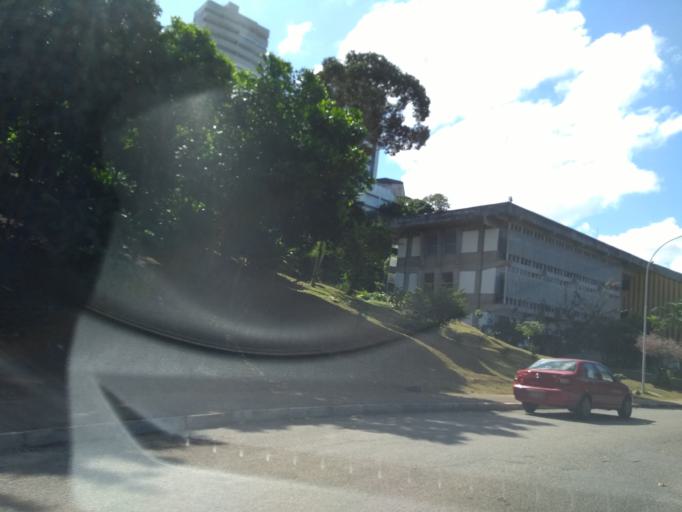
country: BR
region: Bahia
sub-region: Salvador
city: Salvador
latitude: -13.0023
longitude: -38.5105
